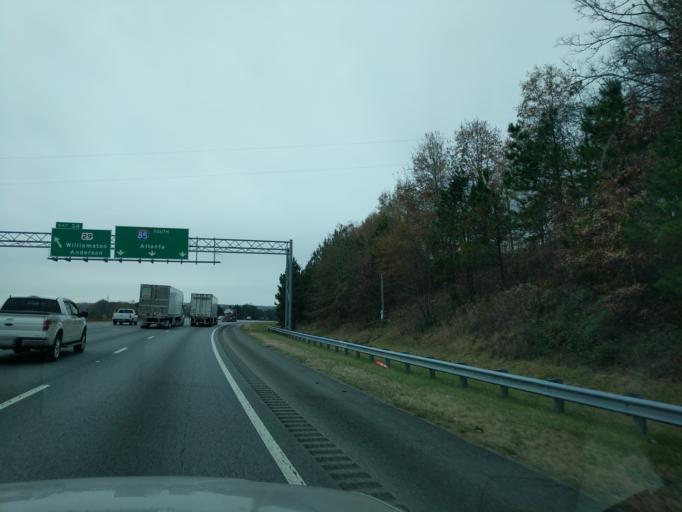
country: US
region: South Carolina
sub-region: Anderson County
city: Piedmont
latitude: 34.6994
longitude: -82.5025
